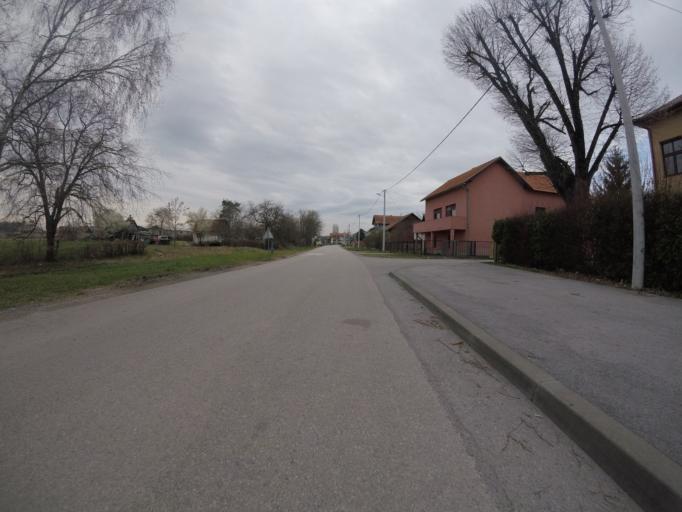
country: HR
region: Zagrebacka
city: Lukavec
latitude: 45.7015
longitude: 15.9925
